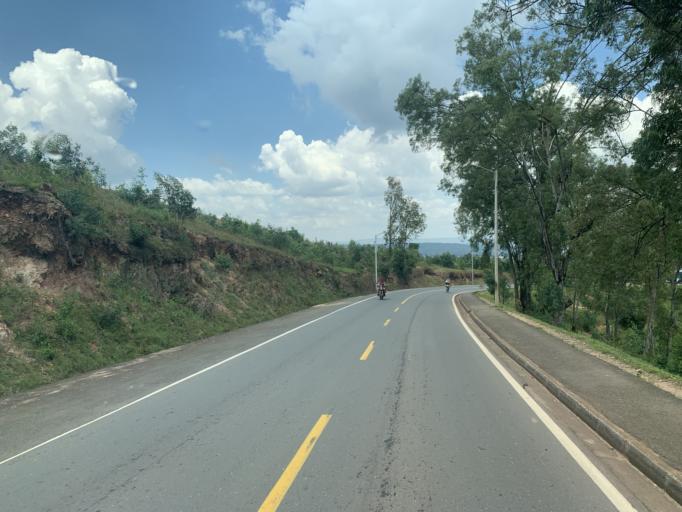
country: RW
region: Kigali
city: Kigali
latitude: -2.0002
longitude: 29.9050
